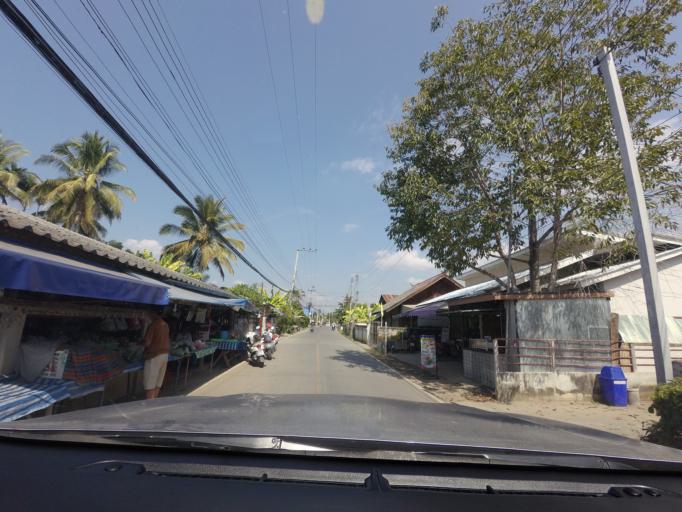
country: TH
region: Mae Hong Son
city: Wiang Nuea
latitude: 19.3772
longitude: 98.4456
